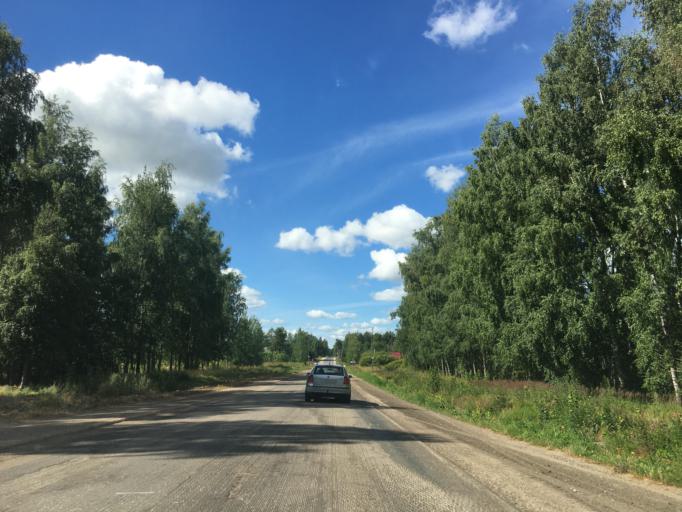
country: RU
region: Pskov
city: Palkino
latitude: 57.5435
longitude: 28.0205
